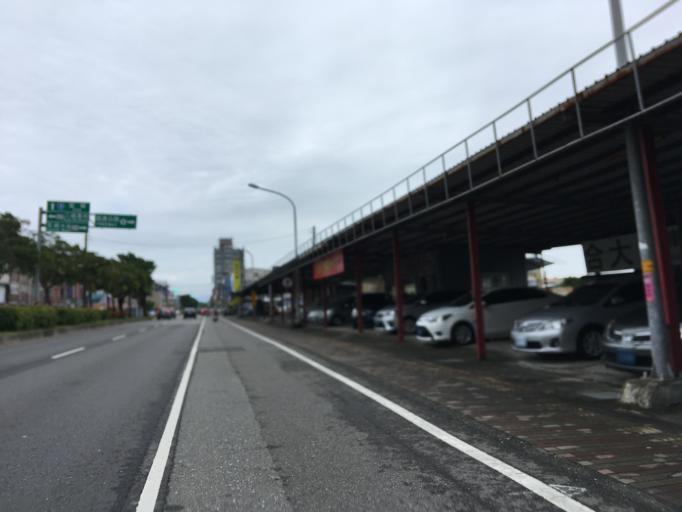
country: TW
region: Taiwan
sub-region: Yilan
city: Yilan
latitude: 24.7042
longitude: 121.7707
